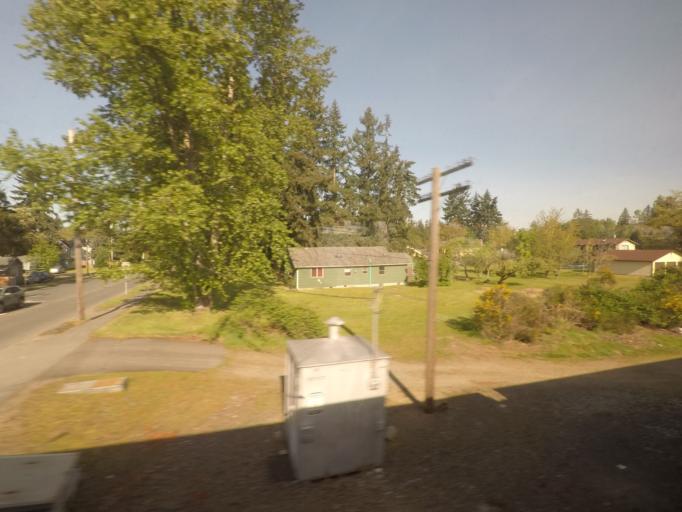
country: US
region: Washington
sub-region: Snohomish County
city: Marysville
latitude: 48.0685
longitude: -122.1775
